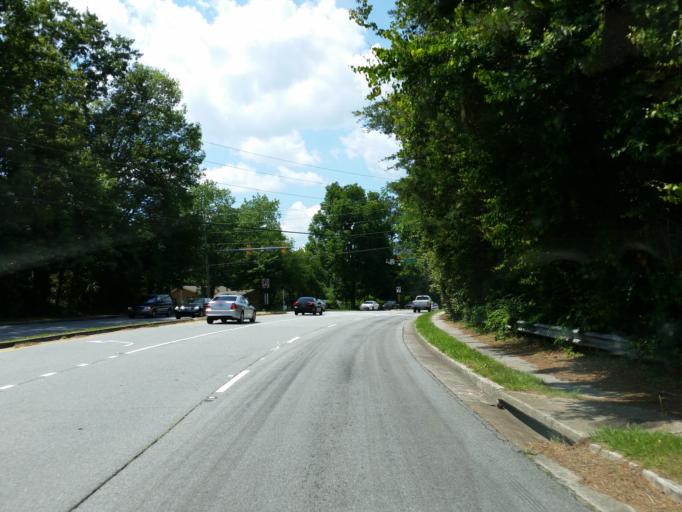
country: US
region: Georgia
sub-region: Cobb County
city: Marietta
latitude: 33.9867
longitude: -84.4875
